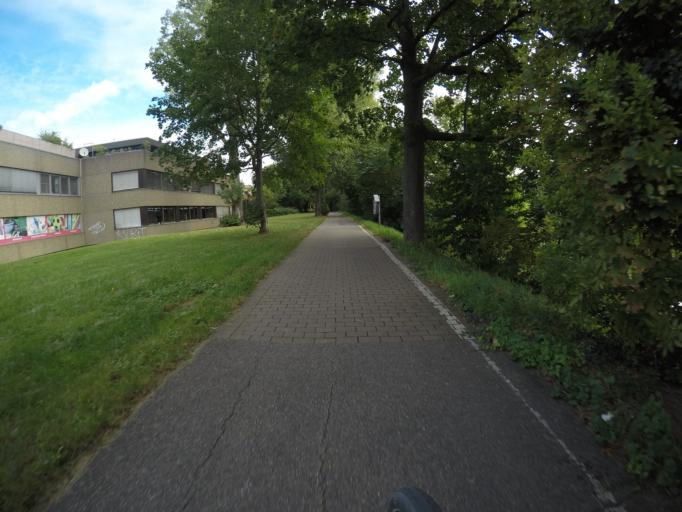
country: DE
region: Baden-Wuerttemberg
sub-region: Regierungsbezirk Stuttgart
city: Stuttgart-Ost
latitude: 48.8105
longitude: 9.2175
